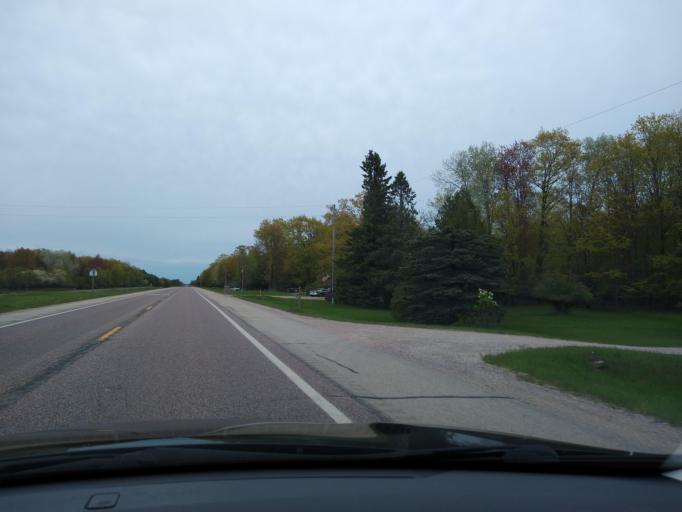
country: US
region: Michigan
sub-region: Delta County
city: Gladstone
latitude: 45.8707
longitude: -87.0636
